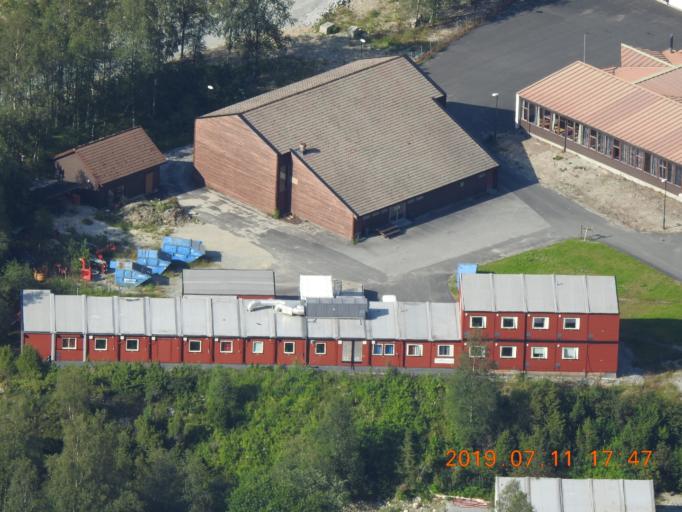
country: NO
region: Vest-Agder
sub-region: Sirdal
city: Tonstad
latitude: 59.0468
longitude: 6.6521
